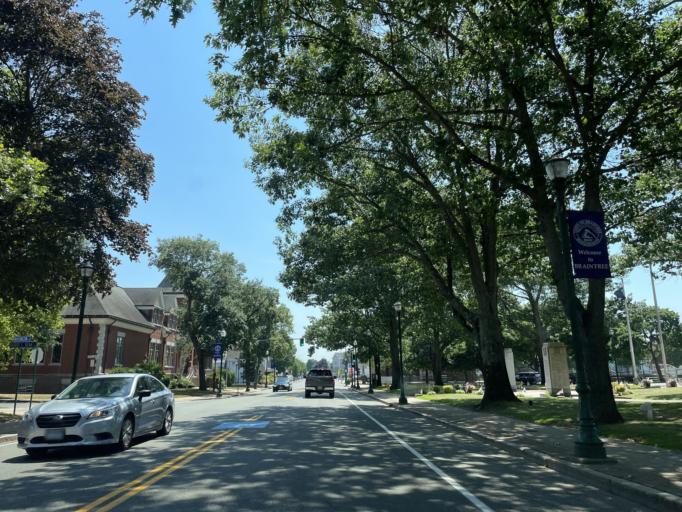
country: US
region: Massachusetts
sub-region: Norfolk County
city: Braintree
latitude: 42.2063
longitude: -71.0044
